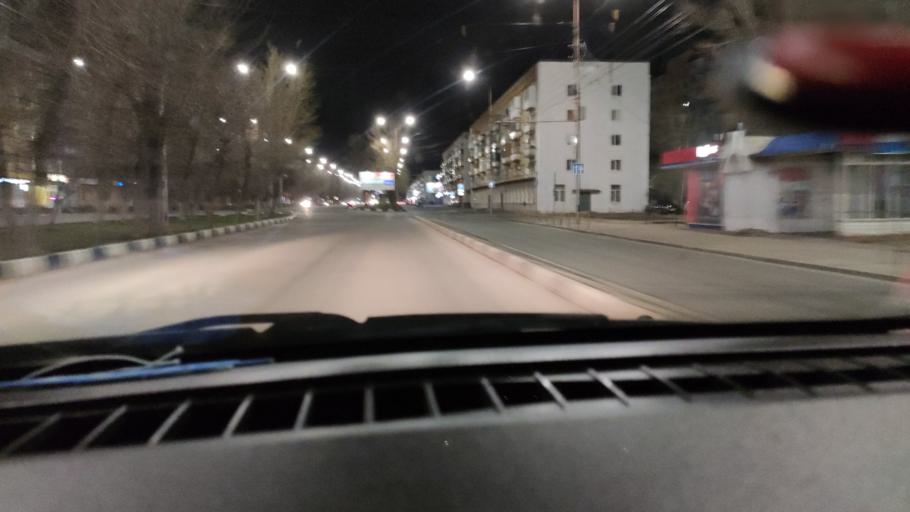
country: RU
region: Saratov
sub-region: Saratovskiy Rayon
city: Saratov
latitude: 51.5959
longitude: 45.9684
